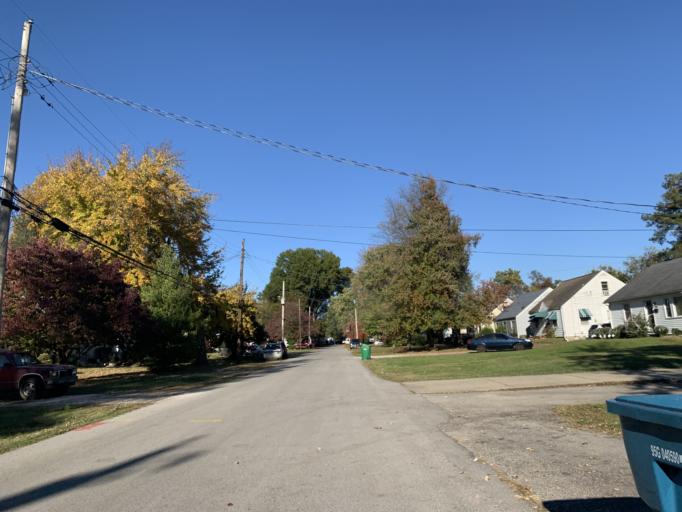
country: US
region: Kentucky
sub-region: Jefferson County
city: Saint Dennis
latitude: 38.1722
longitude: -85.8273
